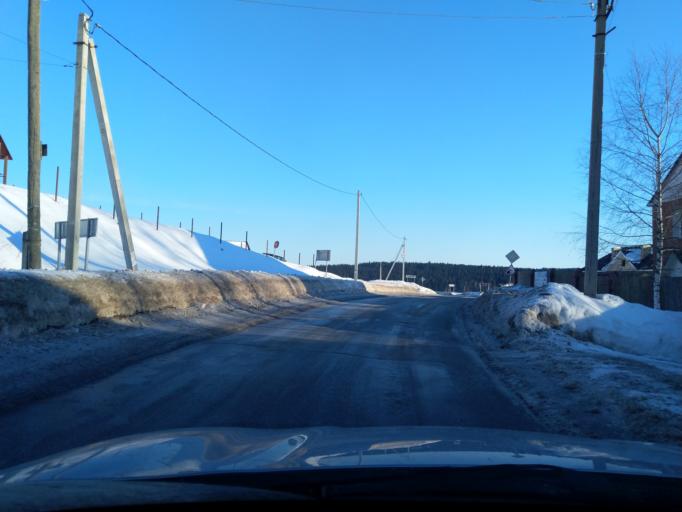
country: RU
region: Perm
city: Polazna
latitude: 58.3068
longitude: 56.4239
